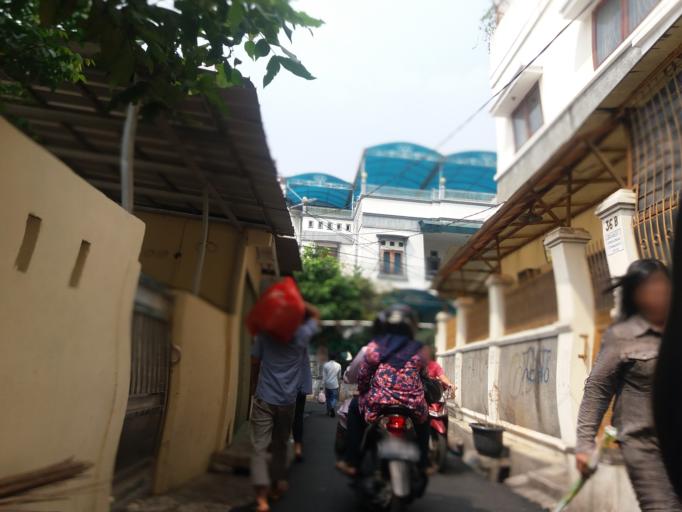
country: ID
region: Jakarta Raya
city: Jakarta
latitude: -6.1893
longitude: 106.8172
